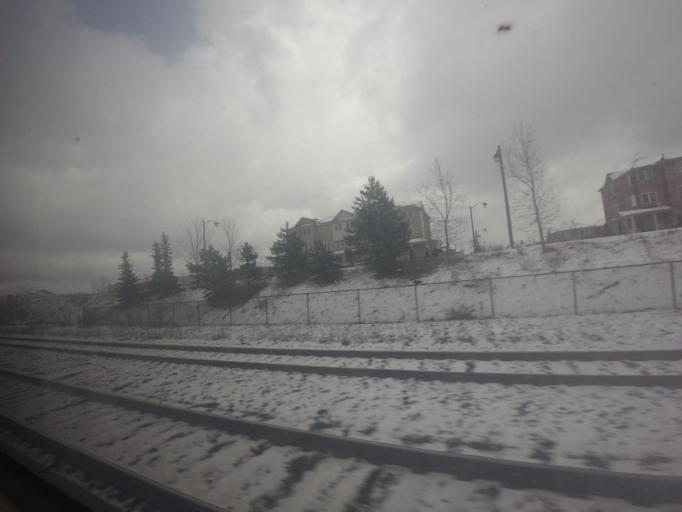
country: CA
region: Ontario
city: Scarborough
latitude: 43.7230
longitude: -79.2510
